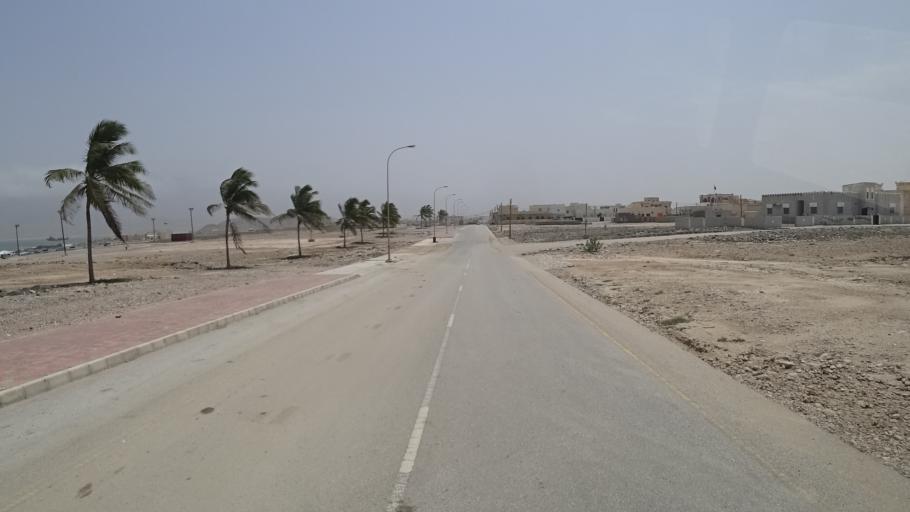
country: OM
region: Zufar
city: Salalah
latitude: 16.9802
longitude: 54.6872
